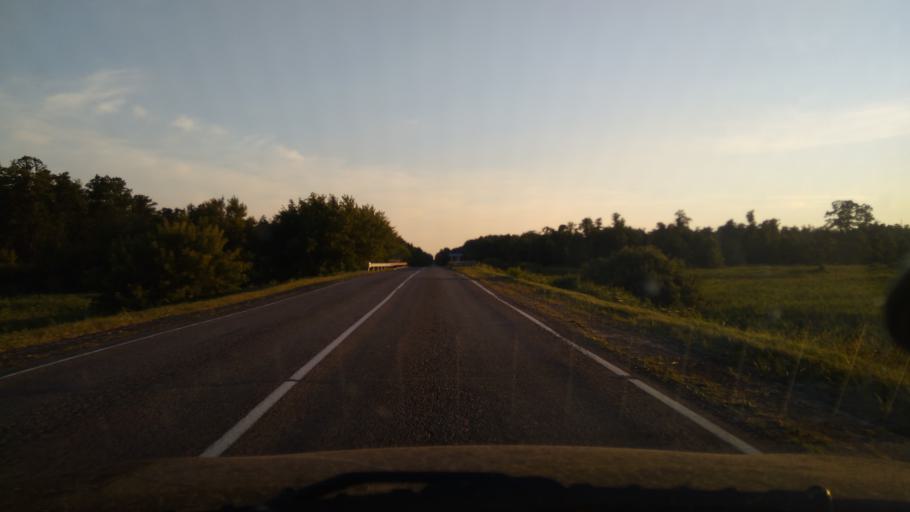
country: BY
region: Brest
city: Nyakhachava
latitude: 52.6167
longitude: 25.1502
